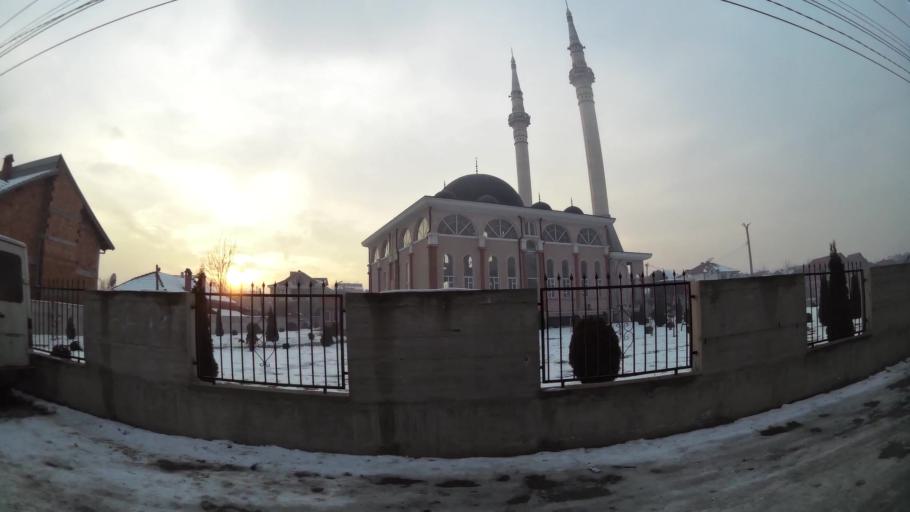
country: MK
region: Suto Orizari
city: Suto Orizare
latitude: 42.0327
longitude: 21.4185
